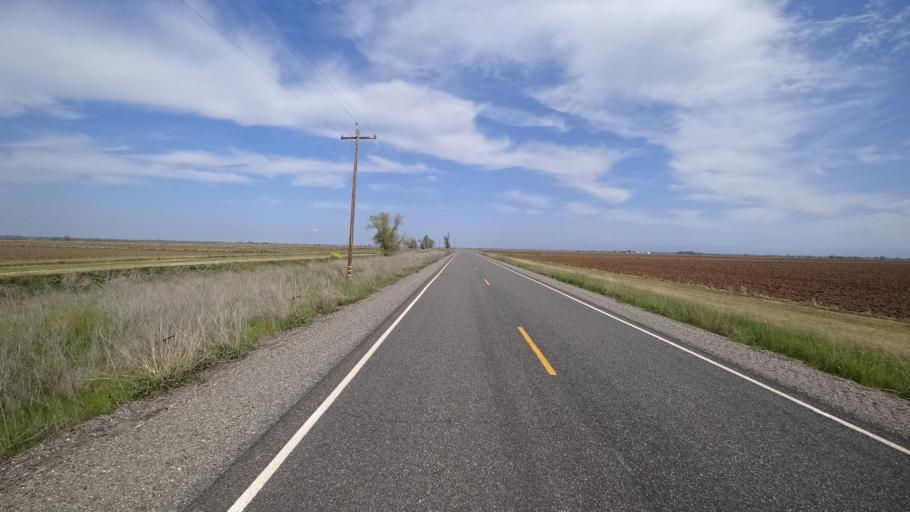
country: US
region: California
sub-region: Butte County
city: Durham
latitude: 39.5190
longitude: -121.9299
